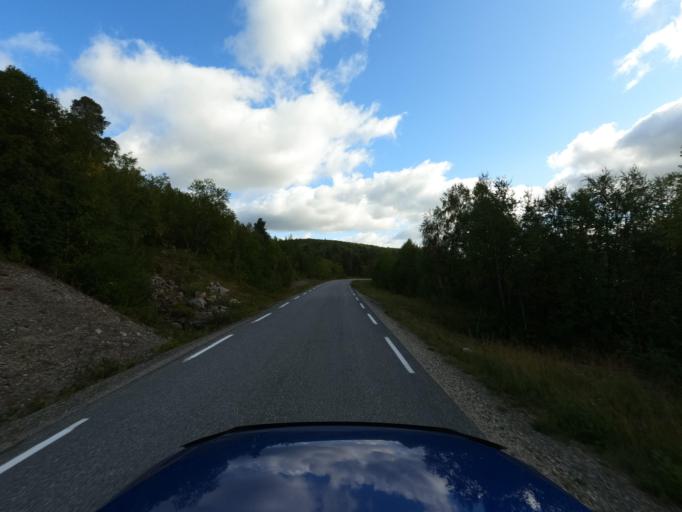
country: NO
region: Finnmark Fylke
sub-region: Karasjok
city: Karasjohka
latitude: 69.4306
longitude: 24.8952
